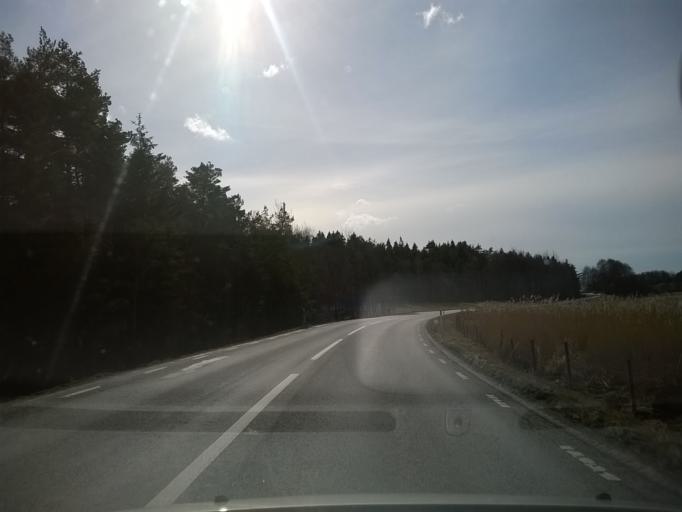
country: SE
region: Vaestra Goetaland
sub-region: Tjorns Kommun
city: Myggenas
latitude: 58.1137
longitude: 11.7033
